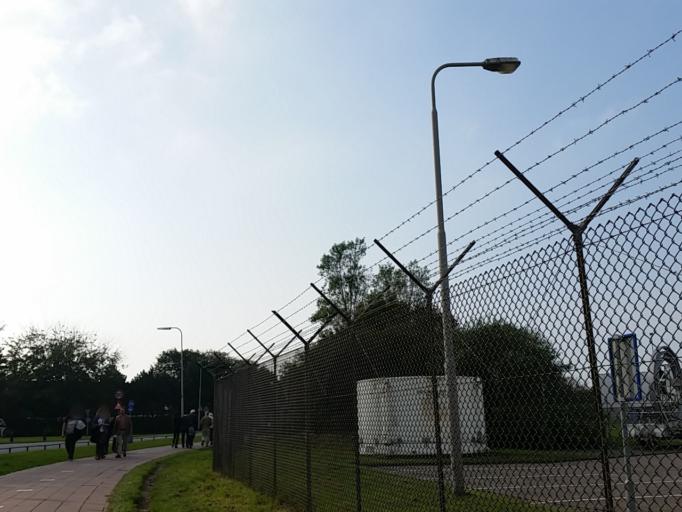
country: NL
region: South Holland
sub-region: Gemeente Katwijk
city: Katwijk aan den Rijn
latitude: 52.2147
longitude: 4.4206
